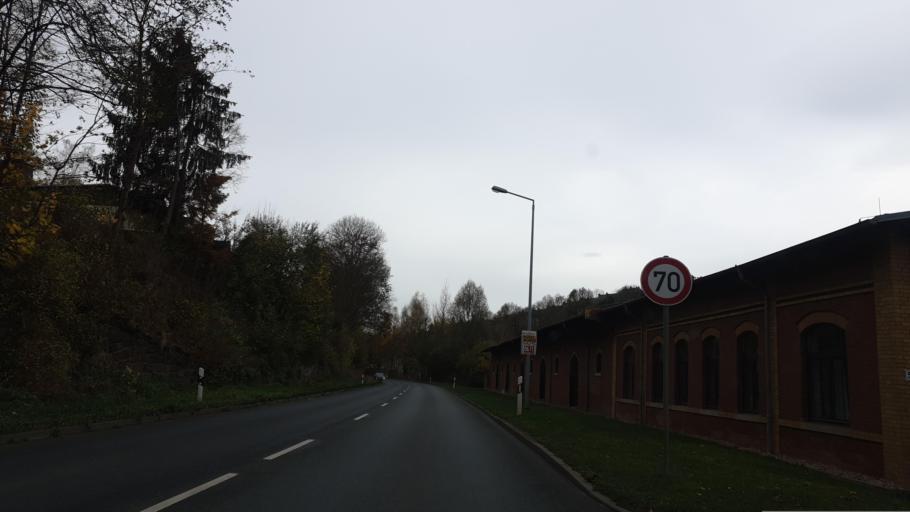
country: DE
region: Saxony
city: Reichenbach/Vogtland
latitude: 50.6189
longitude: 12.2998
